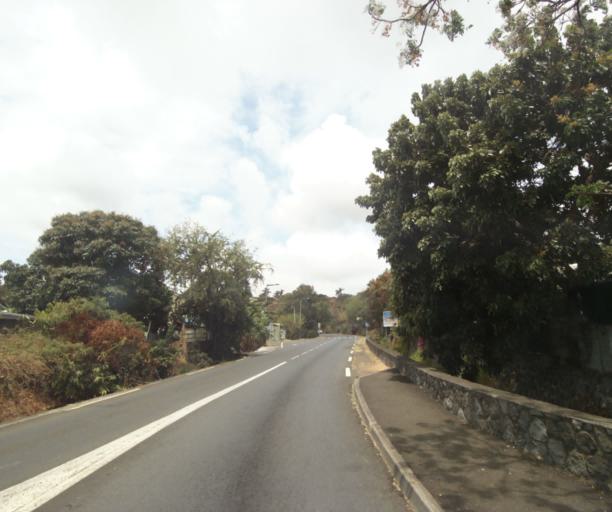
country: RE
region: Reunion
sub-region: Reunion
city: Saint-Paul
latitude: -21.0300
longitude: 55.2658
